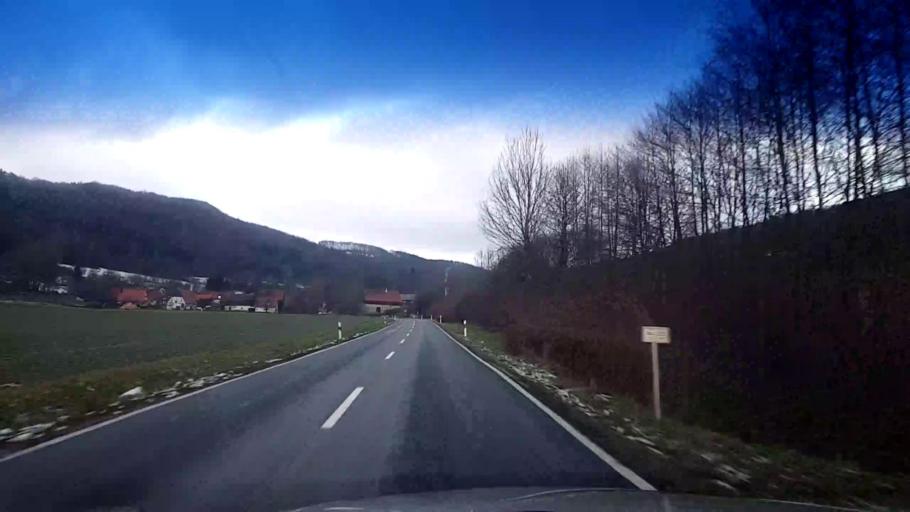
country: DE
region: Bavaria
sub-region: Upper Franconia
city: Buttenheim
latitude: 49.8279
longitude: 11.0792
